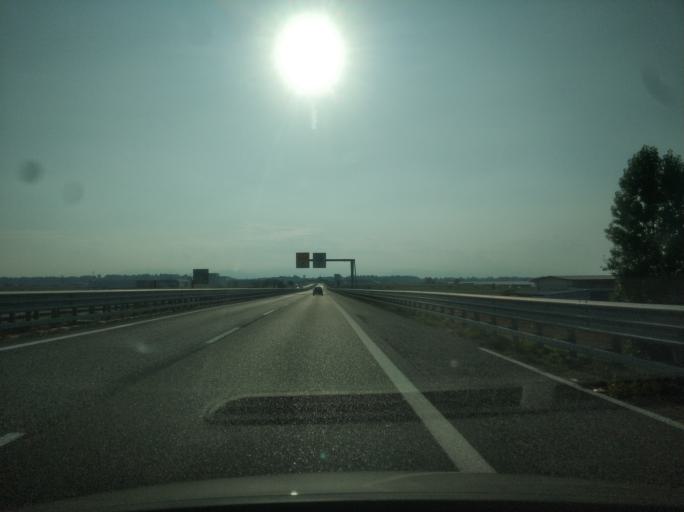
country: IT
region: Piedmont
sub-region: Provincia di Cuneo
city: Cervere
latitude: 44.6646
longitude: 7.7995
